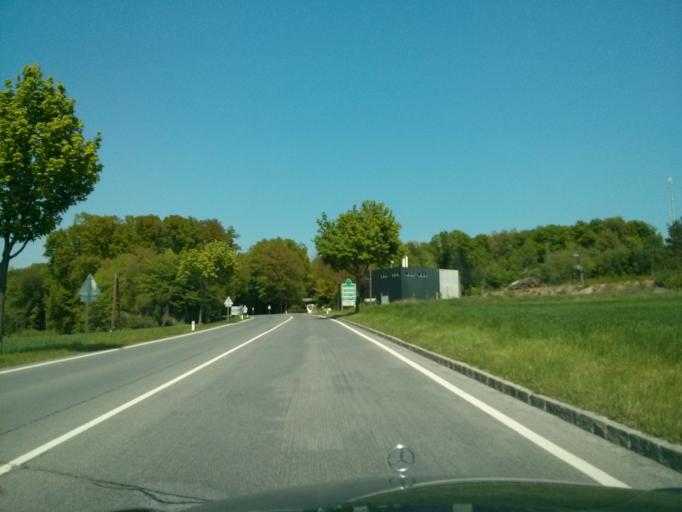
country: AT
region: Burgenland
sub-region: Politischer Bezirk Oberwart
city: Bad Tatzmannsdorf
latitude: 47.3245
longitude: 16.2180
